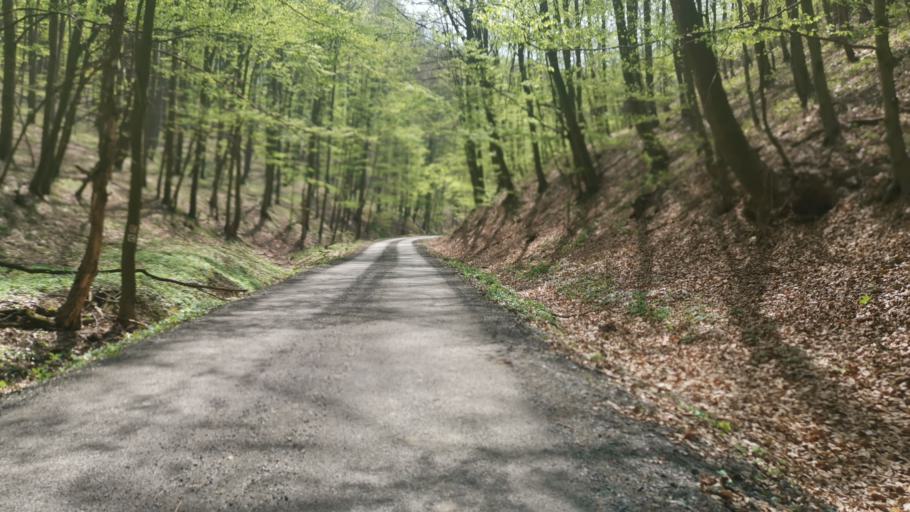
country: SK
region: Nitriansky
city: Brezova pod Bradlom
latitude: 48.5867
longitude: 17.4855
